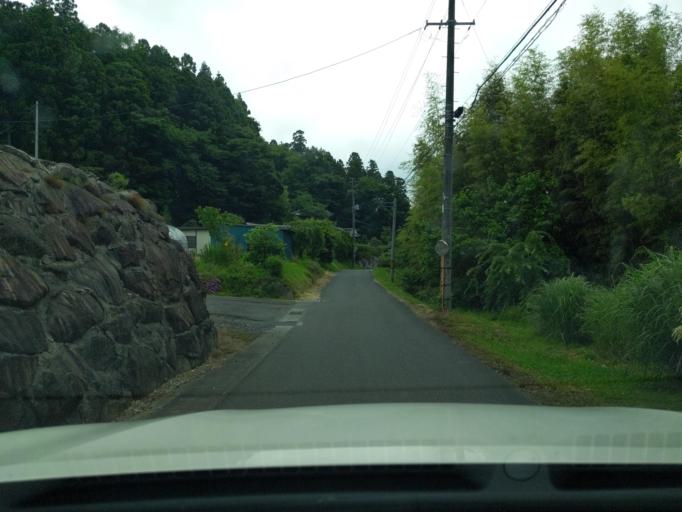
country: JP
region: Fukushima
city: Miharu
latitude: 37.4053
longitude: 140.4441
